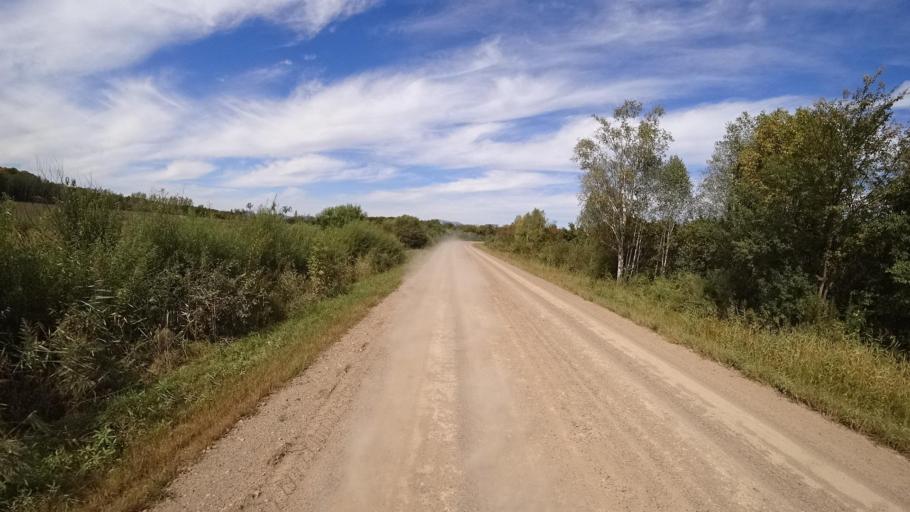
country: RU
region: Primorskiy
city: Yakovlevka
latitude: 44.6168
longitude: 133.5973
